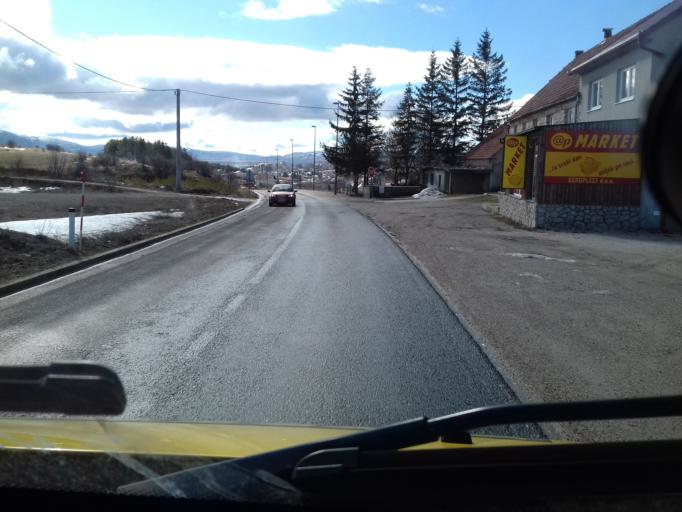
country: BA
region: Federation of Bosnia and Herzegovina
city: Tomislavgrad
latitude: 43.7318
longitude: 17.2220
